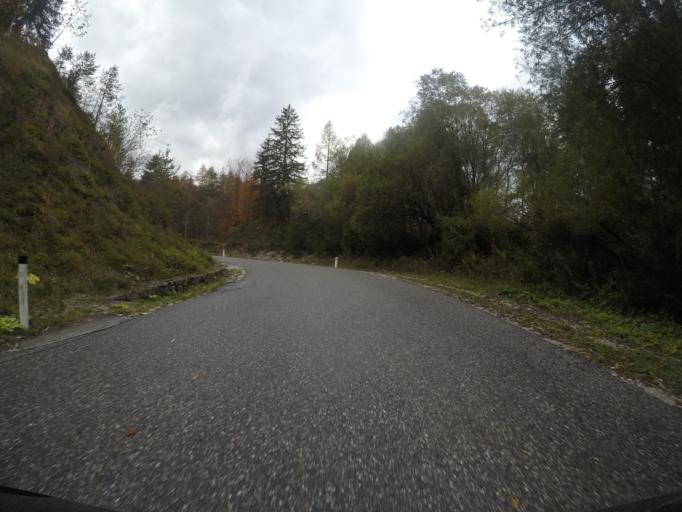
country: SI
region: Kranjska Gora
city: Mojstrana
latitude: 46.4531
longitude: 13.9365
